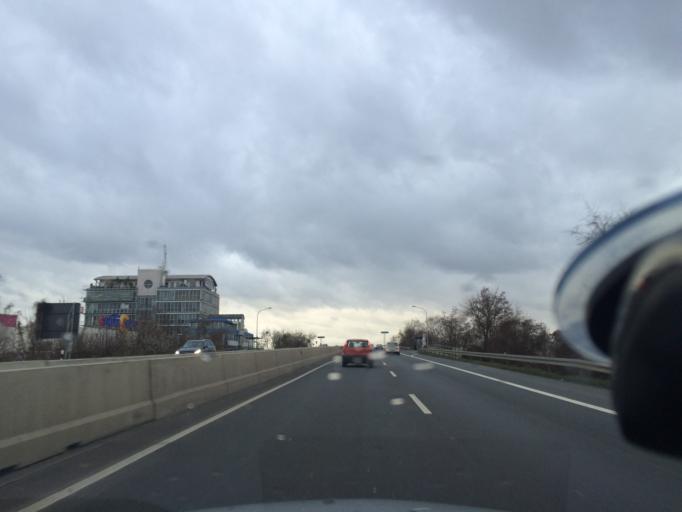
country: DE
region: Hesse
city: Weiterstadt
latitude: 49.8977
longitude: 8.6114
